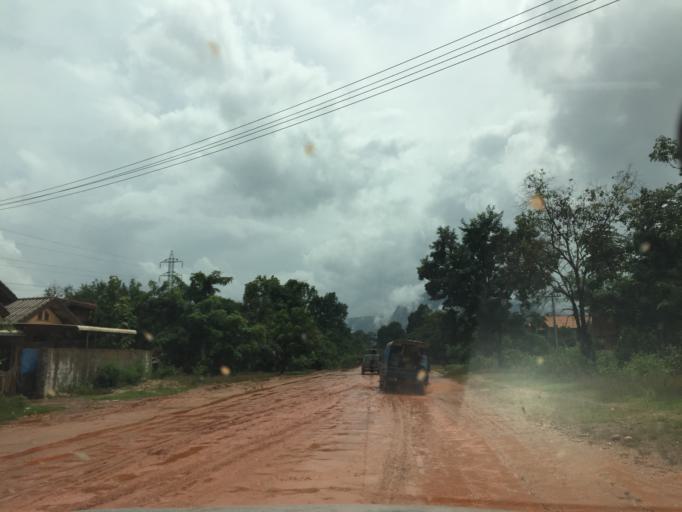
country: LA
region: Attapu
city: Attapu
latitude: 14.8089
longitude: 106.7752
